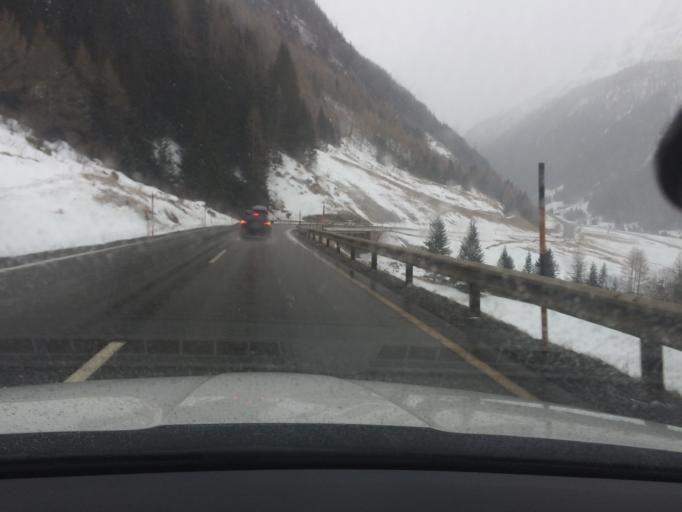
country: AT
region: Tyrol
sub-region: Politischer Bezirk Lienz
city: Matrei in Osttirol
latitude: 47.1166
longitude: 12.5029
